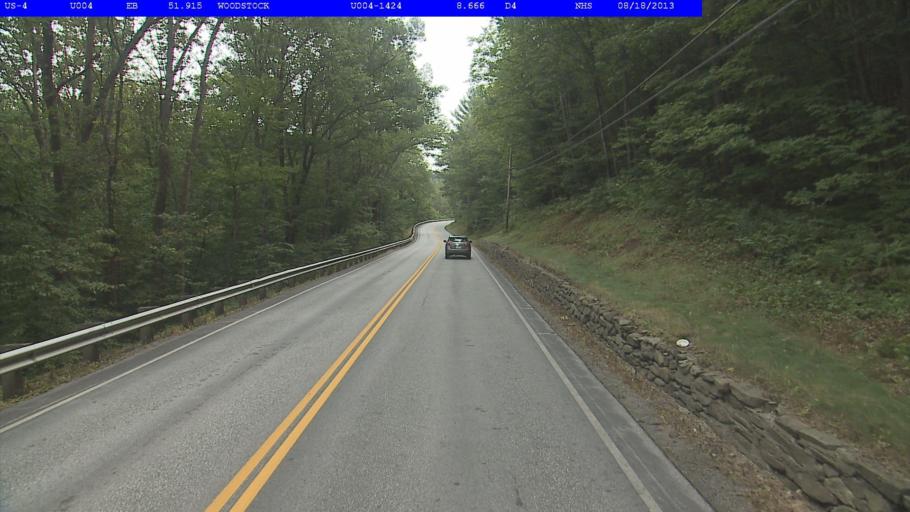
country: US
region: Vermont
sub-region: Windsor County
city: Woodstock
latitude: 43.6383
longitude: -72.4804
